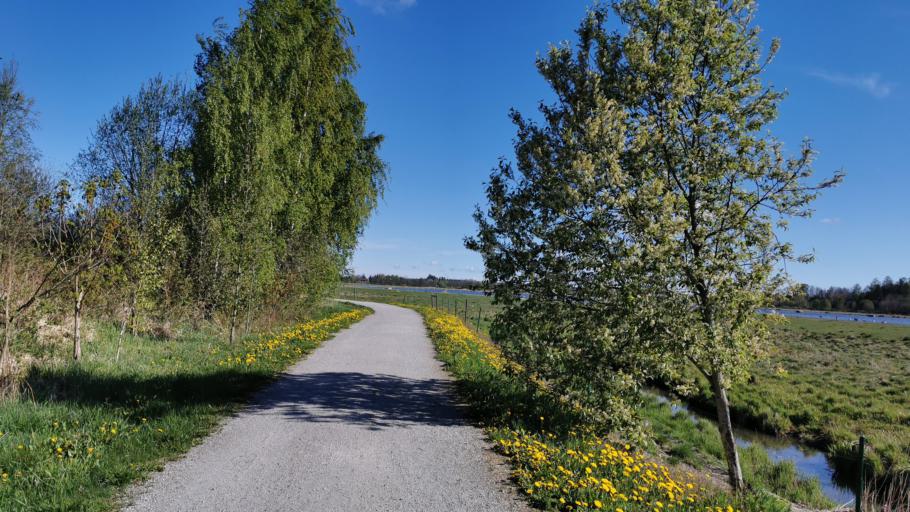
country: SE
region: OErebro
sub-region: Orebro Kommun
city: Orebro
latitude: 59.2976
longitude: 15.2135
